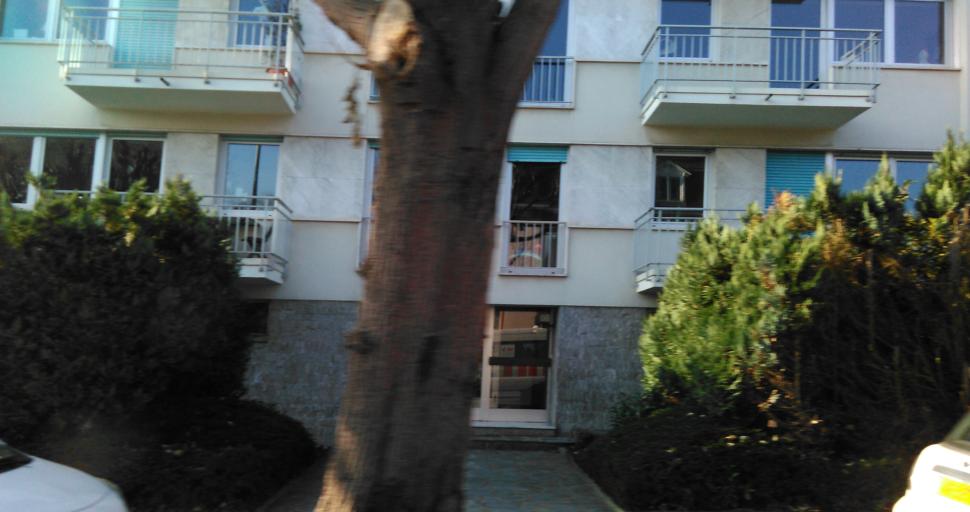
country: LU
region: Luxembourg
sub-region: Canton de Luxembourg
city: Luxembourg
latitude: 49.6090
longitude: 6.1209
